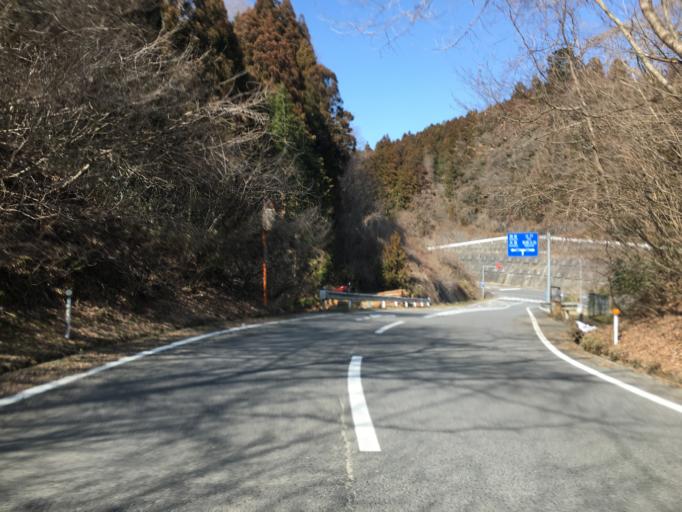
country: JP
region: Ibaraki
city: Daigo
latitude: 36.7942
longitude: 140.4746
